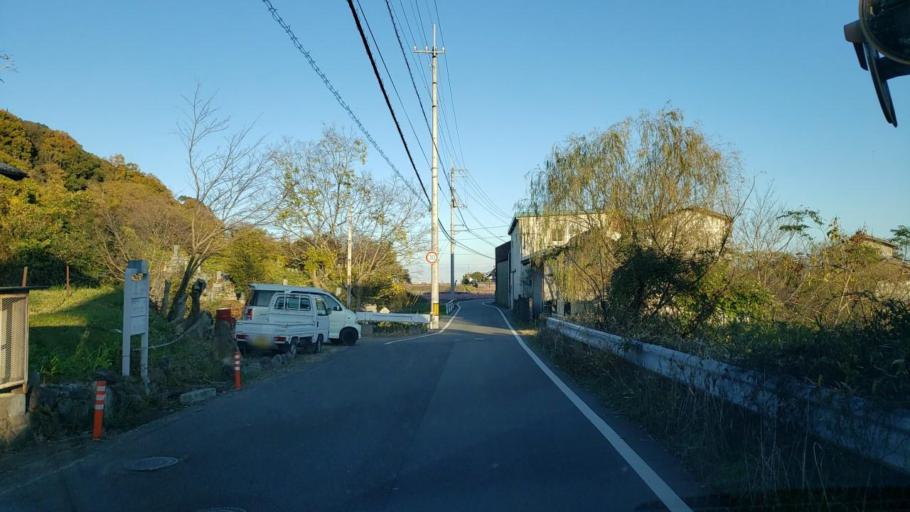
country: JP
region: Tokushima
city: Kamojimacho-jogejima
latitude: 34.1009
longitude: 134.3115
